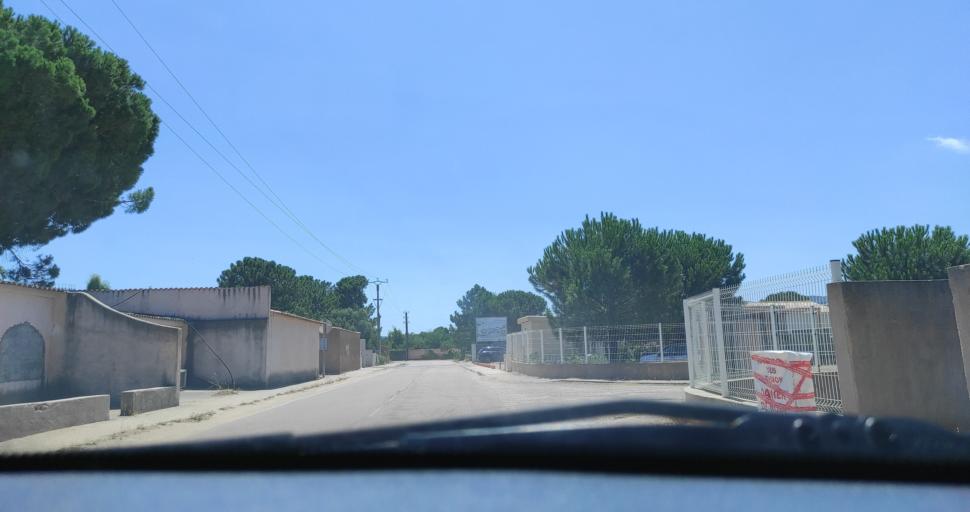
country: FR
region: Corsica
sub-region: Departement de la Corse-du-Sud
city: Porto-Vecchio
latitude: 41.6288
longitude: 9.3343
